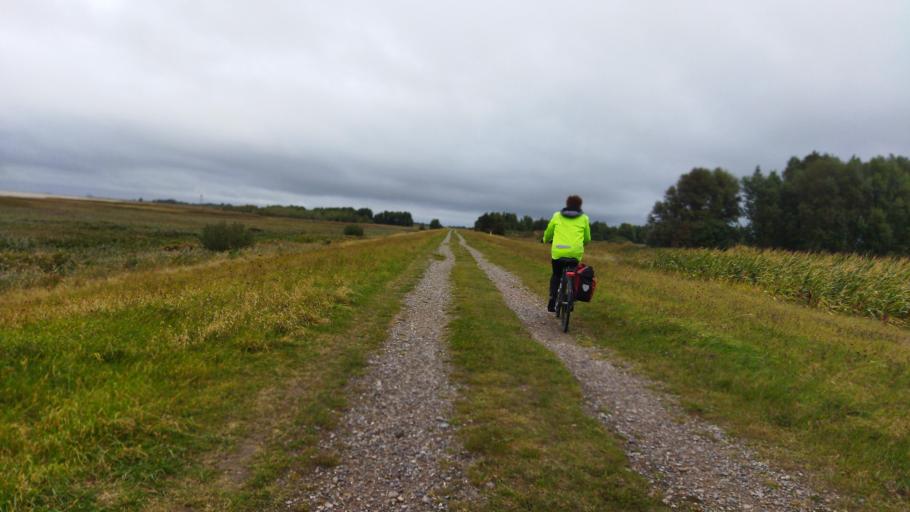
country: NL
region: Groningen
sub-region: Gemeente Delfzijl
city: Delfzijl
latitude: 53.3718
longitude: 7.0090
